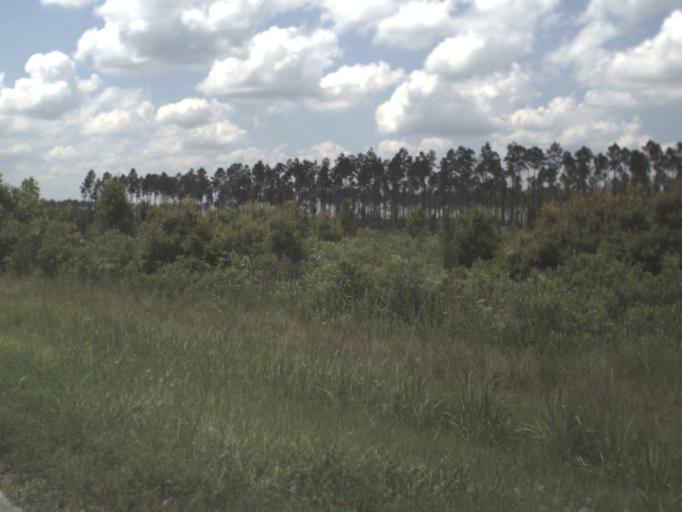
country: US
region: Florida
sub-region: Baker County
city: Macclenny
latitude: 30.5449
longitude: -82.3463
